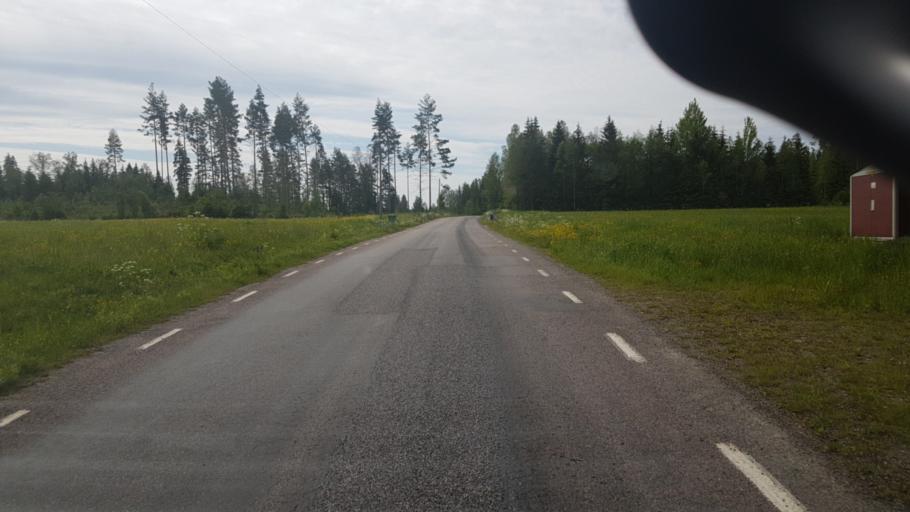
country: SE
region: Vaermland
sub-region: Eda Kommun
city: Charlottenberg
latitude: 59.8658
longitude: 12.3455
